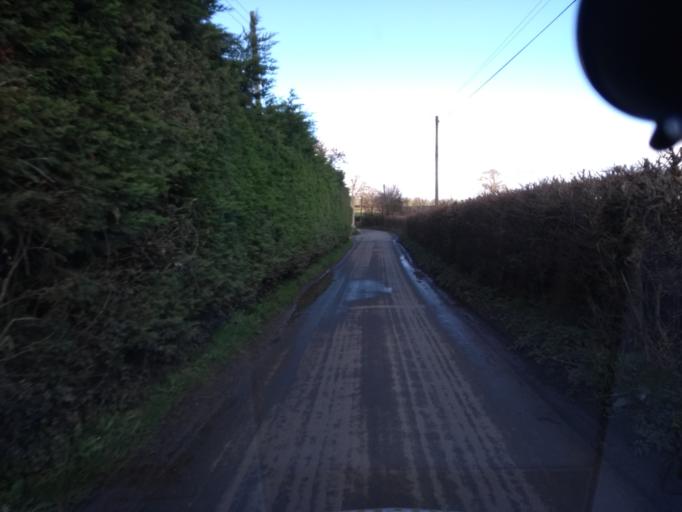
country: GB
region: England
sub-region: Somerset
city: Creech Saint Michael
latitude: 50.9682
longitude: -3.0140
